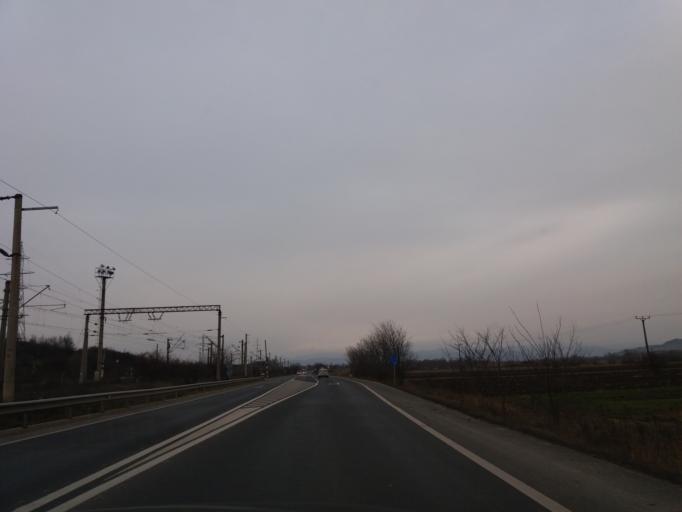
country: RO
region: Hunedoara
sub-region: Comuna Calan
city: Calan
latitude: 45.7628
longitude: 23.0003
